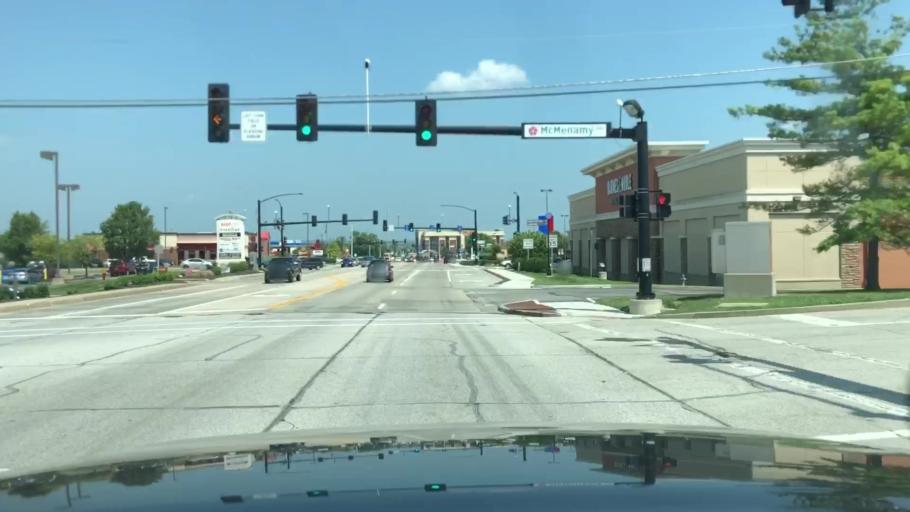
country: US
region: Missouri
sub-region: Saint Charles County
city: Saint Peters
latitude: 38.7938
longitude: -90.6230
